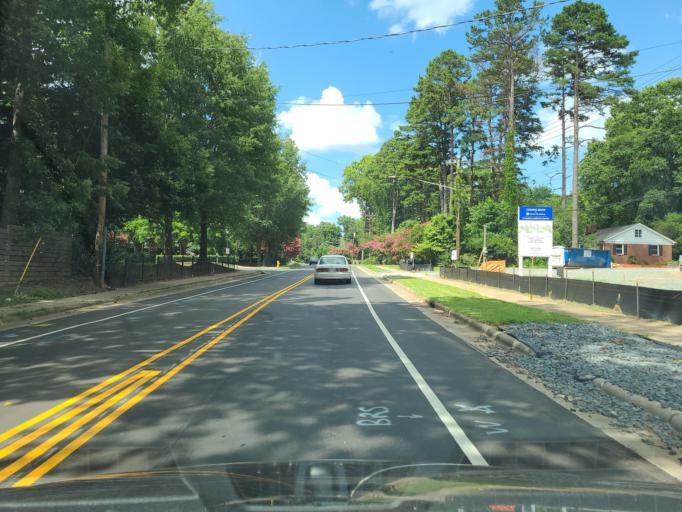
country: US
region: North Carolina
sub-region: Mecklenburg County
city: Charlotte
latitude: 35.2129
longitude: -80.7907
